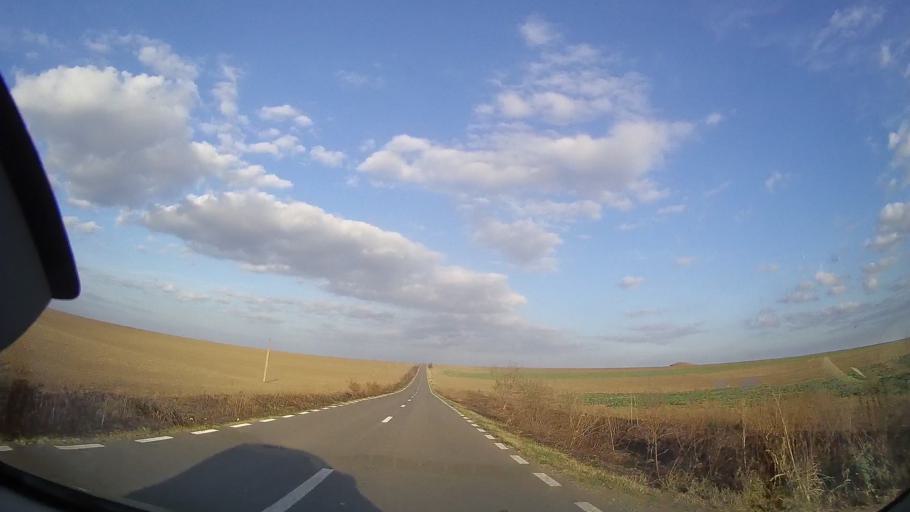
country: RO
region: Constanta
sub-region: Comuna Independenta
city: Independenta
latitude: 43.9412
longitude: 28.0495
